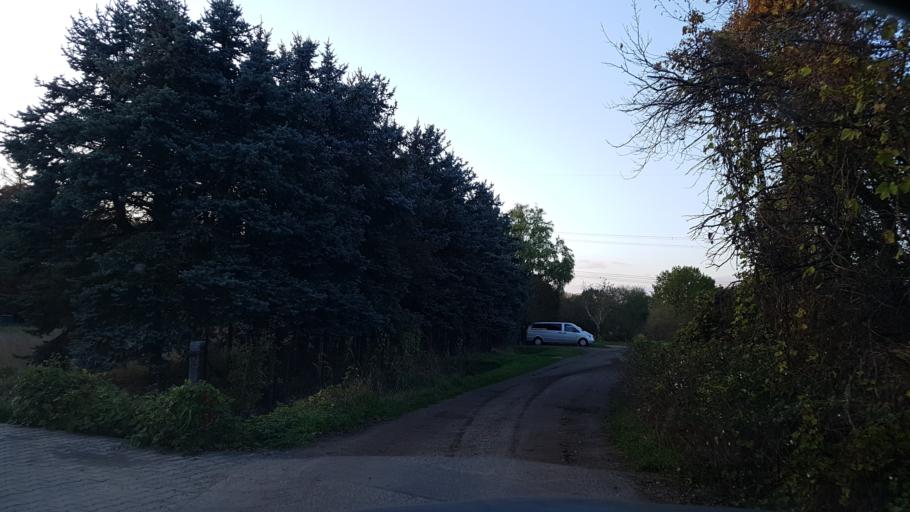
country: DE
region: Brandenburg
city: Doberlug-Kirchhain
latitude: 51.6442
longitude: 13.5634
